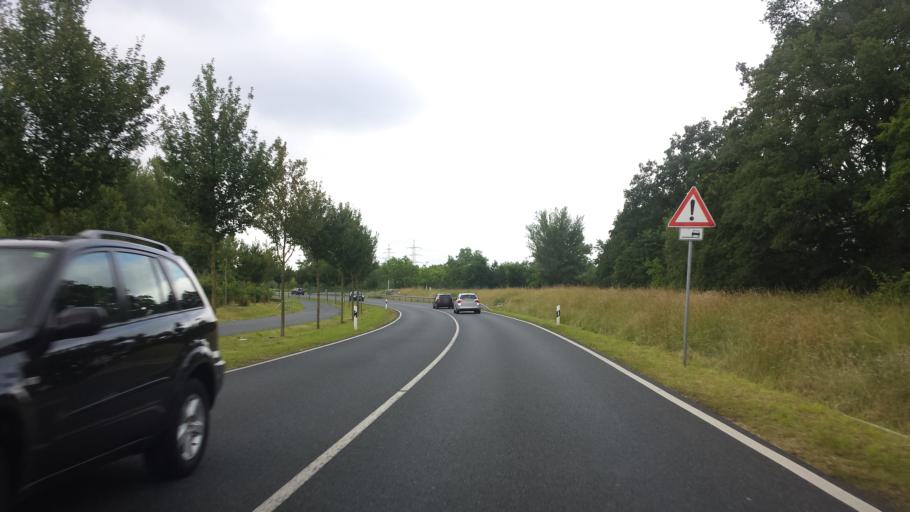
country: DE
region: Hesse
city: Kelsterbach
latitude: 50.0881
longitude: 8.5531
